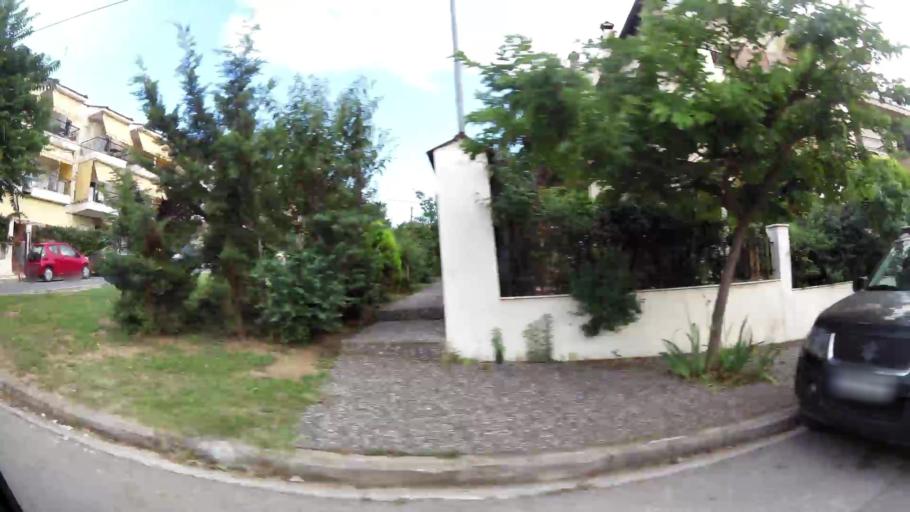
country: GR
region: Central Macedonia
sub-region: Nomos Thessalonikis
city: Pefka
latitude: 40.6604
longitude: 22.9905
